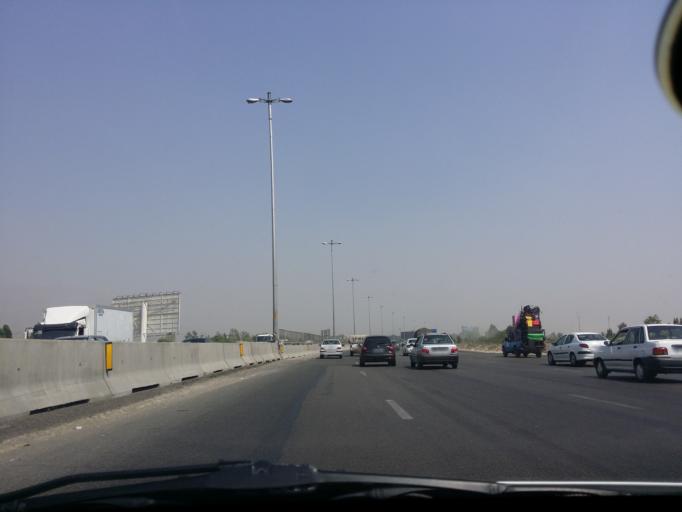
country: IR
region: Alborz
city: Karaj
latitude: 35.8092
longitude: 50.9616
